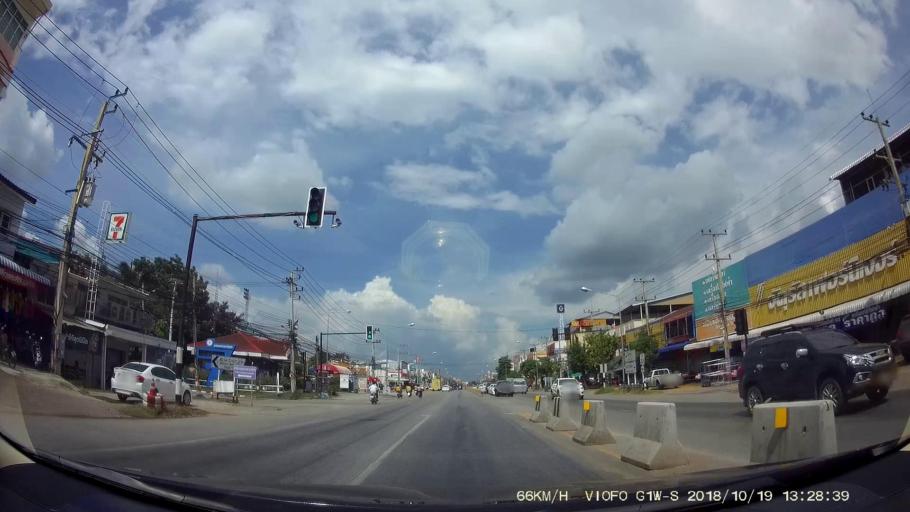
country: TH
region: Chaiyaphum
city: Chatturat
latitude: 15.5639
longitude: 101.8497
